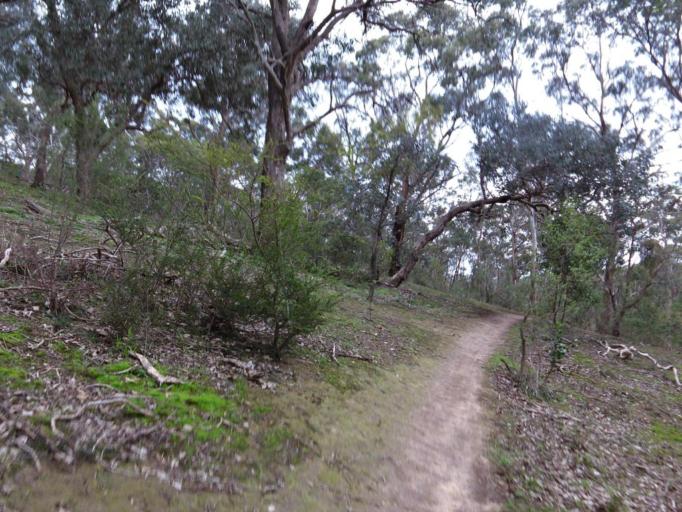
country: AU
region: Victoria
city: Plenty
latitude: -37.6741
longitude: 145.0978
